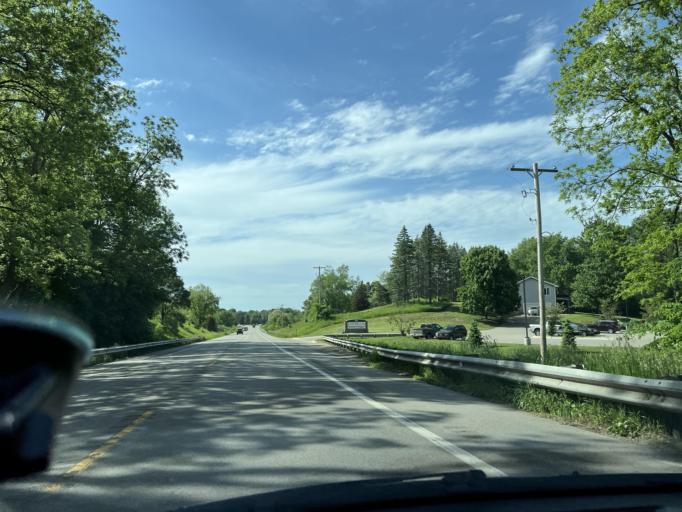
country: US
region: Michigan
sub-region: Barry County
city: Hastings
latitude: 42.6491
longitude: -85.3391
